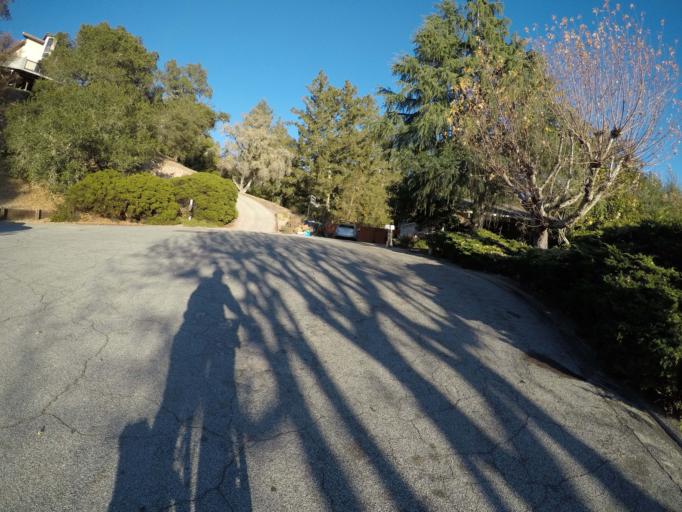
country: US
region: California
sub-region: Santa Cruz County
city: Scotts Valley
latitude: 37.0767
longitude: -121.9974
